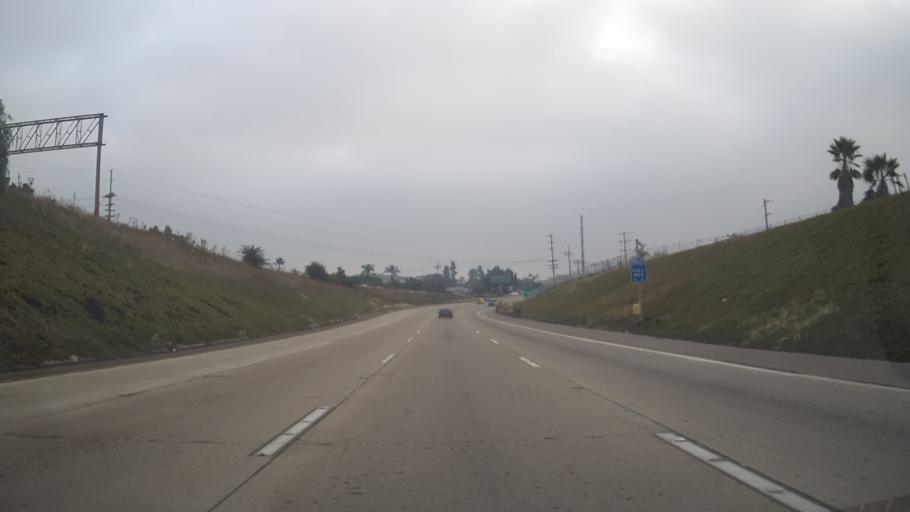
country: US
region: California
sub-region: San Diego County
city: Lemon Grove
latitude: 32.7423
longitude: -117.0469
